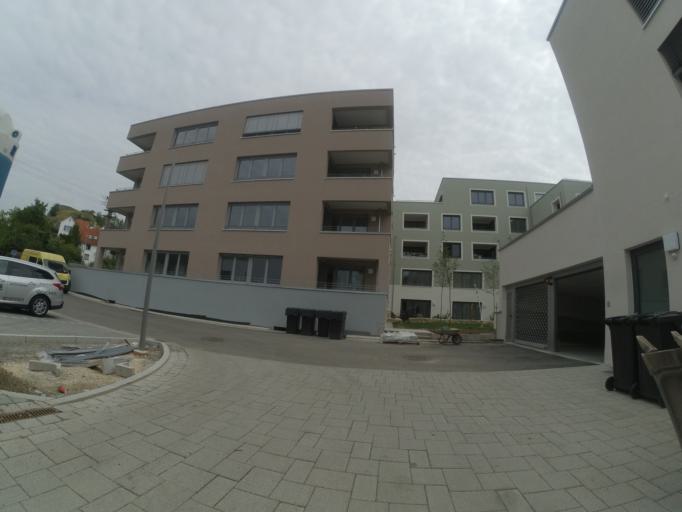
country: DE
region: Baden-Wuerttemberg
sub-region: Tuebingen Region
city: Dornstadt
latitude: 48.4148
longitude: 9.9225
